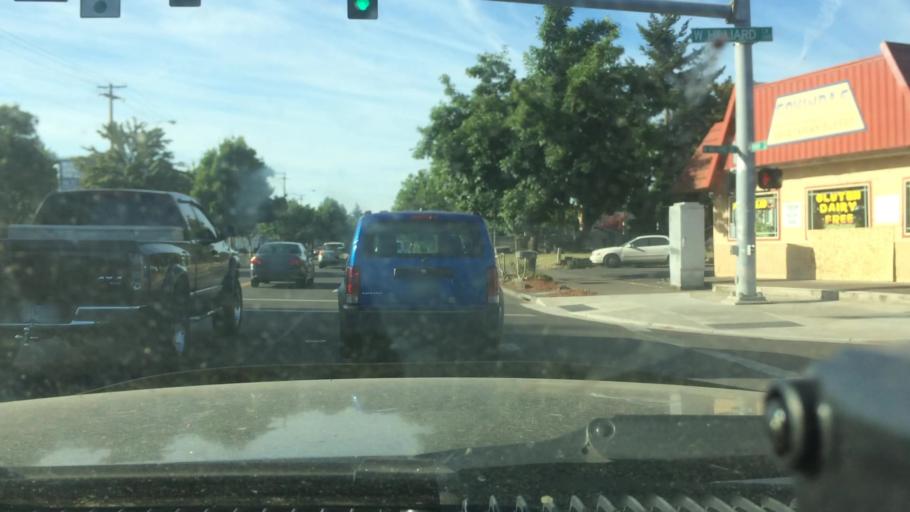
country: US
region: Oregon
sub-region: Lane County
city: Eugene
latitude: 44.0790
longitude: -123.1212
